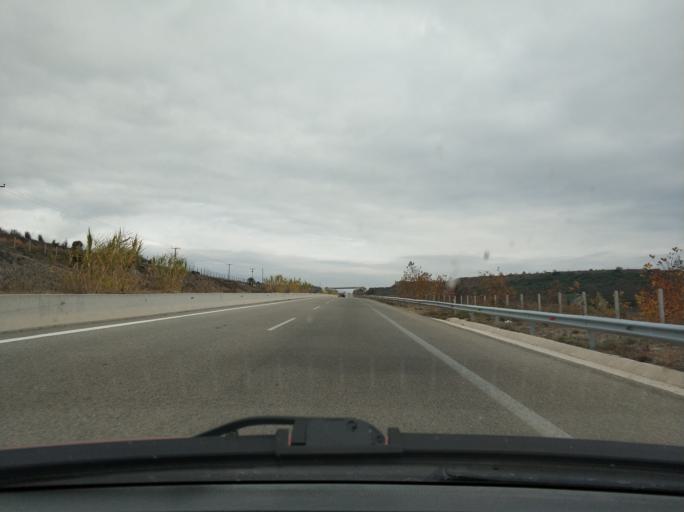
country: GR
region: East Macedonia and Thrace
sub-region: Nomos Kavalas
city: Paralia Ofryniou
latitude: 40.7951
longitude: 24.0088
